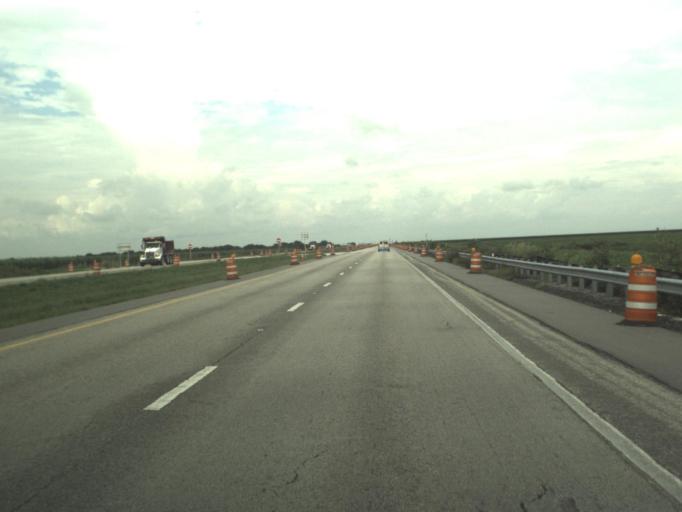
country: US
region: Florida
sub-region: Palm Beach County
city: Belle Glade
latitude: 26.7258
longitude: -80.4964
